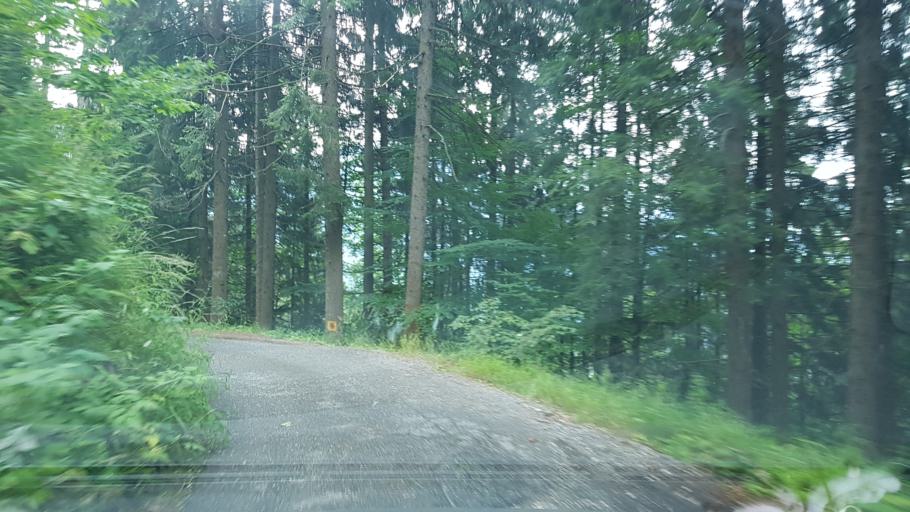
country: IT
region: Friuli Venezia Giulia
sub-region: Provincia di Udine
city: Cercivento
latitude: 46.5360
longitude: 12.9847
